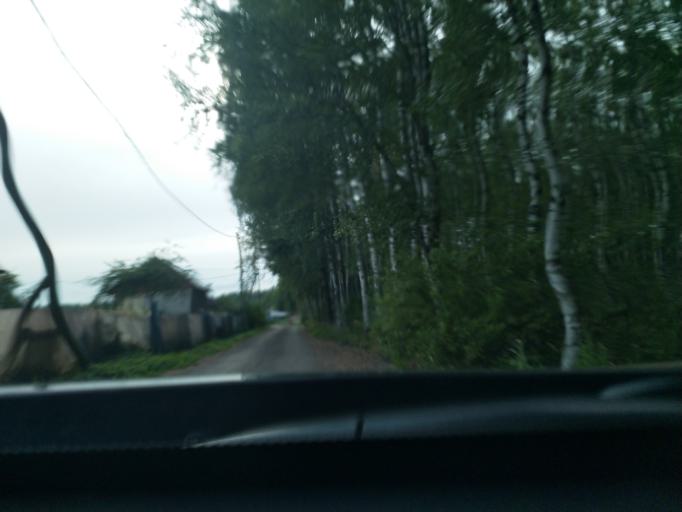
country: RU
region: Leningrad
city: Nikol'skoye
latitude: 59.7267
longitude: 30.7718
